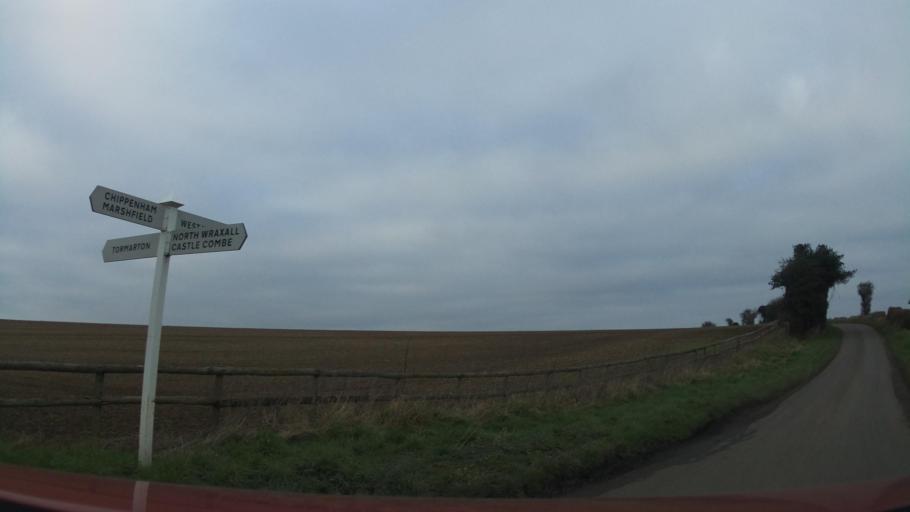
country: GB
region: England
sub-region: Wiltshire
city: Nettleton
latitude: 51.4798
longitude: -2.2861
